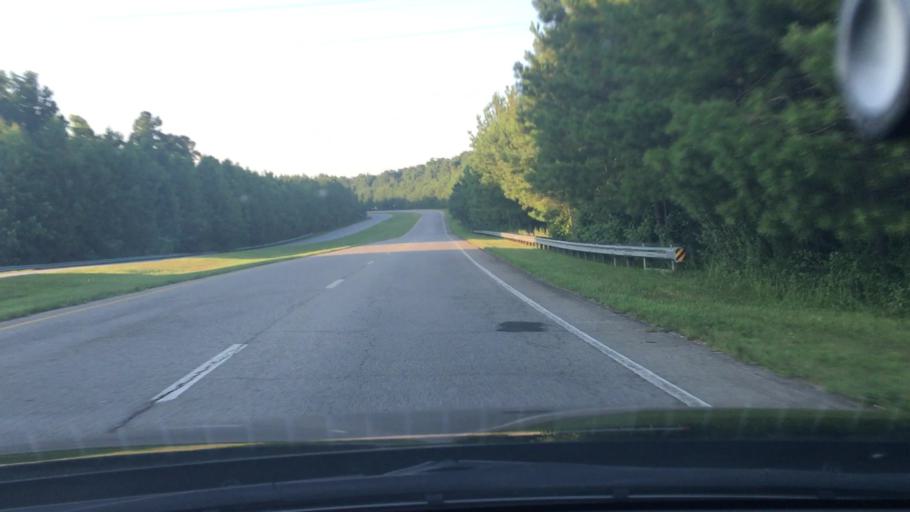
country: US
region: Georgia
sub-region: Coweta County
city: East Newnan
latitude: 33.3663
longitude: -84.7649
